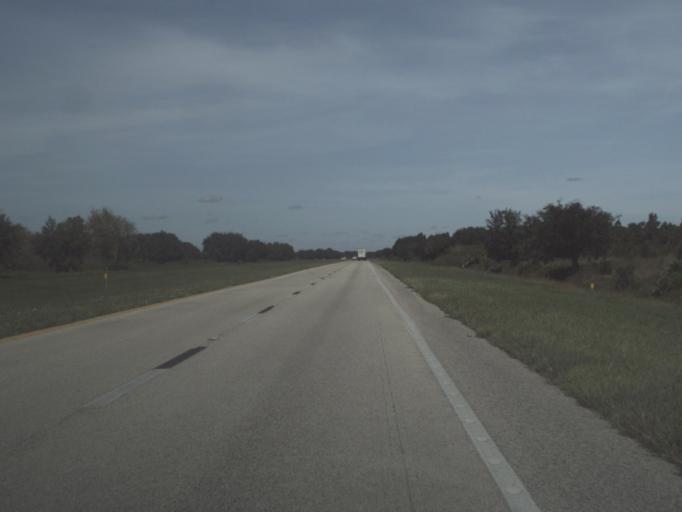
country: US
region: Florida
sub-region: Highlands County
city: Placid Lakes
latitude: 27.0136
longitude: -81.3352
